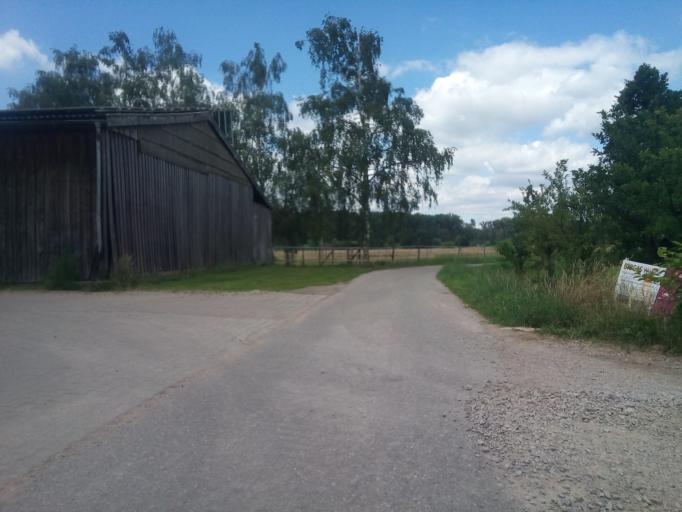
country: DE
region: Baden-Wuerttemberg
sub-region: Freiburg Region
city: Renchen
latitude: 48.6224
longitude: 7.9739
